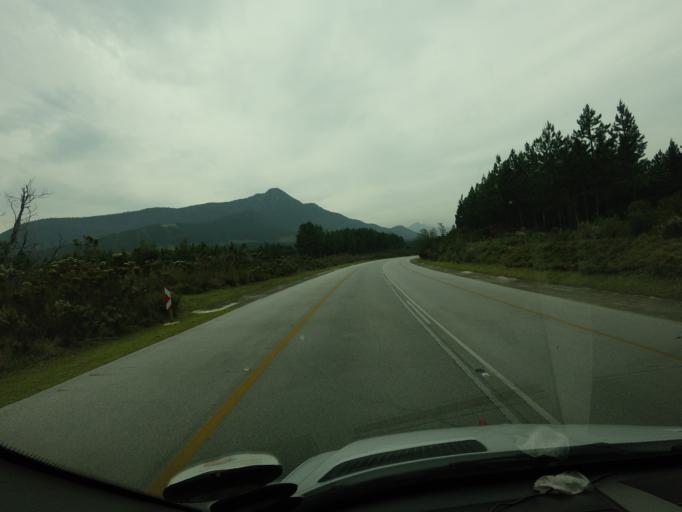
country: ZA
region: Eastern Cape
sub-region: Cacadu District Municipality
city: Kareedouw
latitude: -33.9652
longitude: 23.8666
